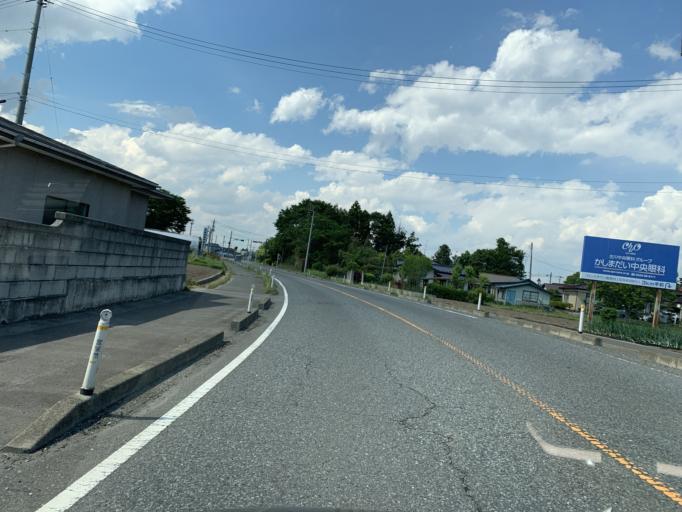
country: JP
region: Miyagi
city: Wakuya
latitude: 38.5009
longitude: 141.1200
